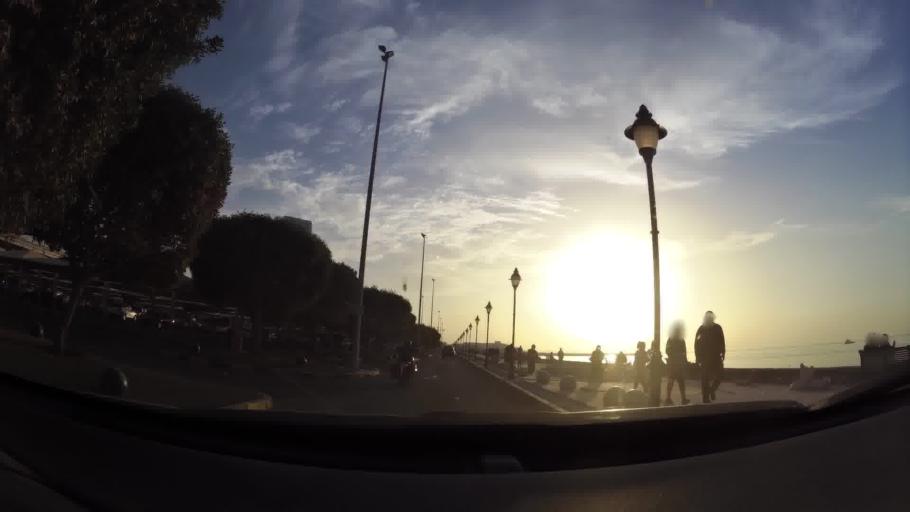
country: KW
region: Al Asimah
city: Kuwait City
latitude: 29.3890
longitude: 47.9791
